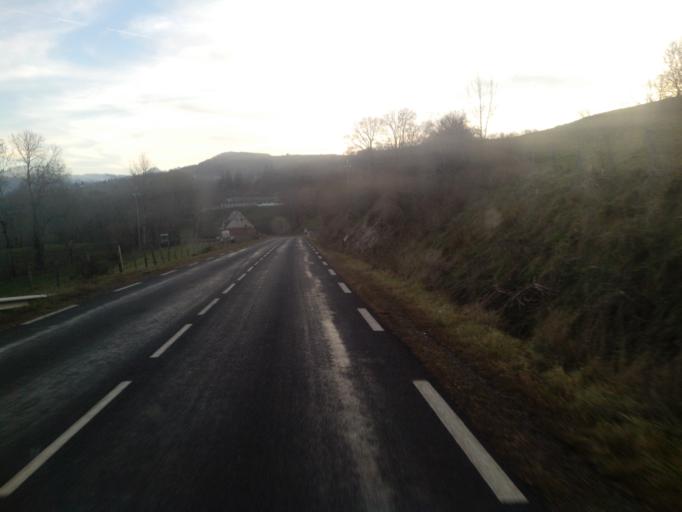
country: FR
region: Auvergne
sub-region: Departement du Cantal
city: Riom-es-Montagnes
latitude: 45.2519
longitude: 2.7065
